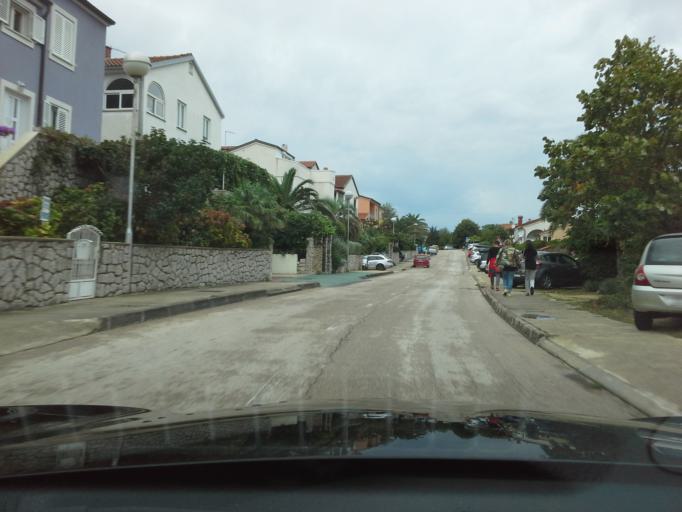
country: HR
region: Primorsko-Goranska
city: Mali Losinj
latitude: 44.5338
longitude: 14.4744
